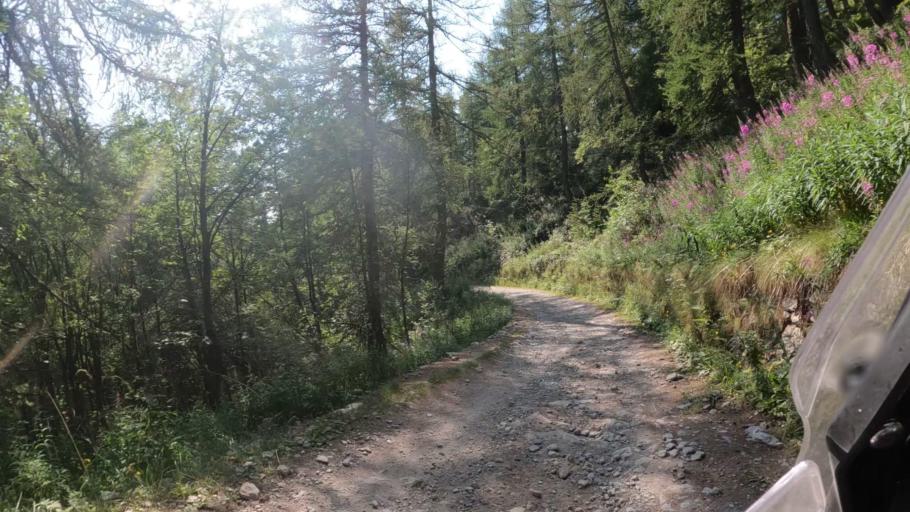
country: IT
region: Piedmont
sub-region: Provincia di Cuneo
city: Briga Alta
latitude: 44.0964
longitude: 7.7195
